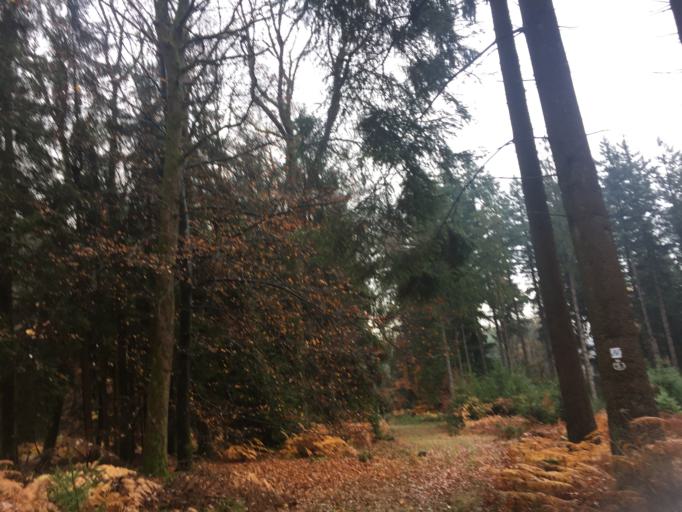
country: DE
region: Hesse
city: Hirschhorn
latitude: 49.4389
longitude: 8.8740
